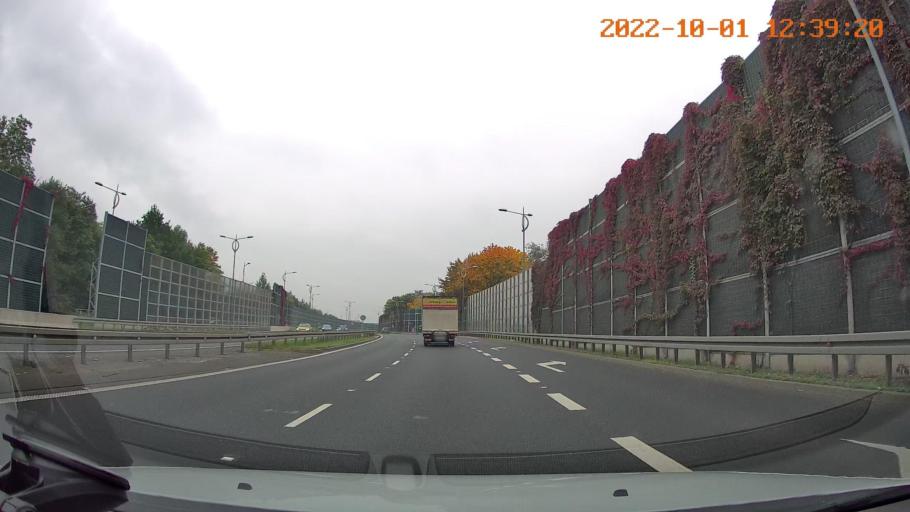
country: PL
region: Silesian Voivodeship
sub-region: Tychy
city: Cielmice
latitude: 50.1156
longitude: 19.0115
